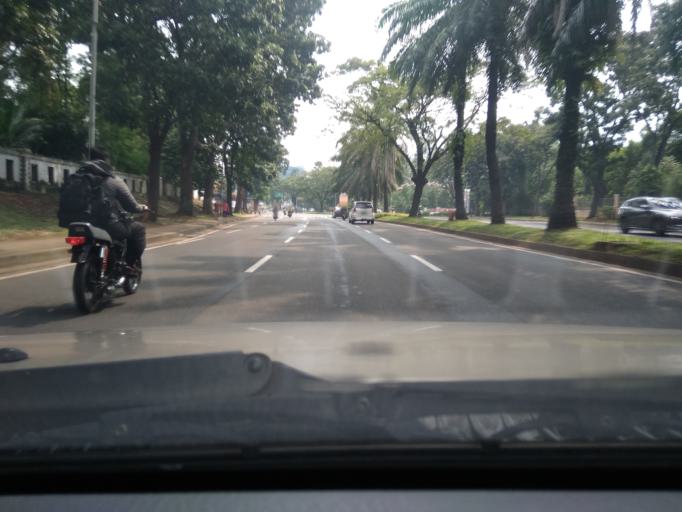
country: ID
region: West Java
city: Serpong
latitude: -6.2838
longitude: 106.6695
